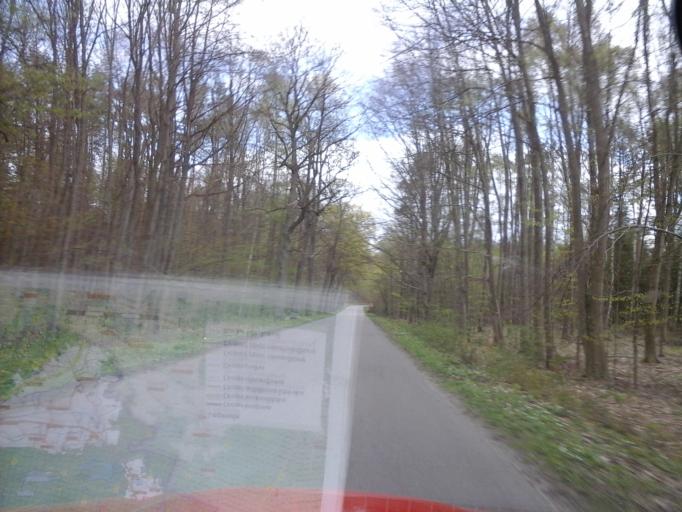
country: PL
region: West Pomeranian Voivodeship
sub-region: Powiat choszczenski
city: Bierzwnik
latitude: 53.0156
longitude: 15.6415
